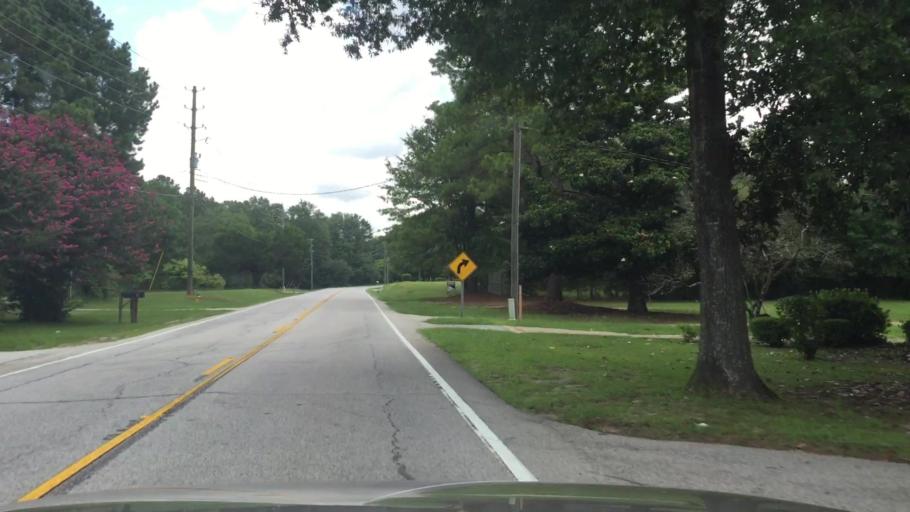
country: US
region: South Carolina
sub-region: Sumter County
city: South Sumter
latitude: 33.9125
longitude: -80.3969
